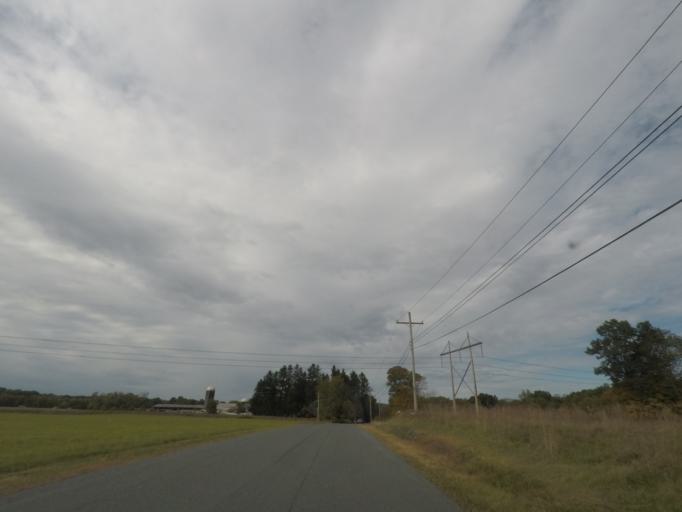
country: US
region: New York
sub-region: Rensselaer County
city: Nassau
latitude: 42.5514
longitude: -73.6244
